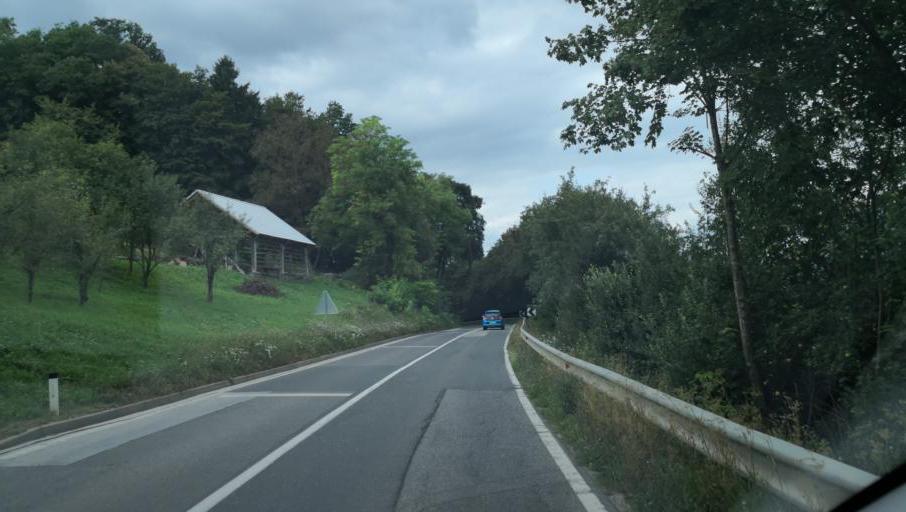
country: SI
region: Novo Mesto
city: Novo Mesto
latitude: 45.7764
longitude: 15.1855
